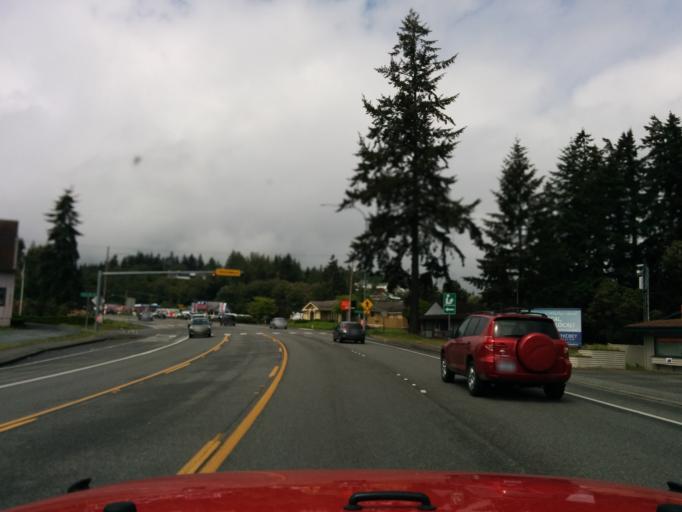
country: US
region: Washington
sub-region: Snohomish County
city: Mukilteo
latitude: 47.9794
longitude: -122.3573
